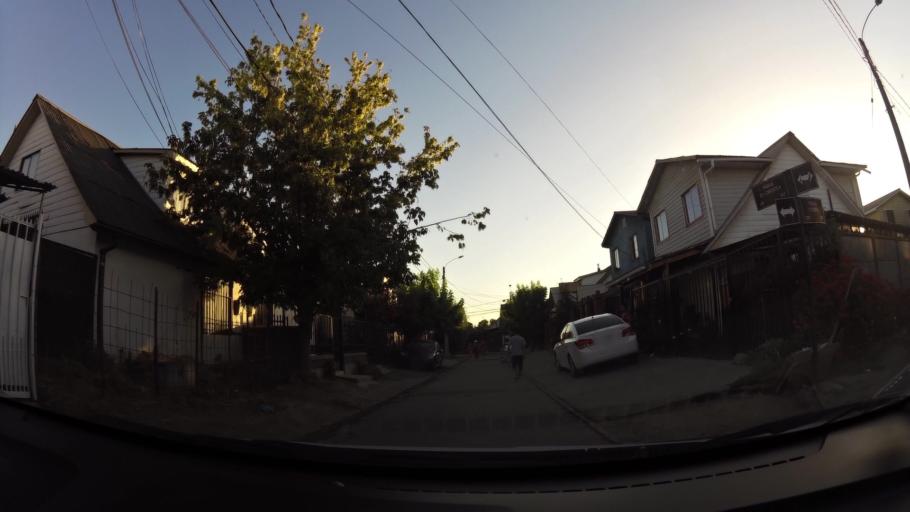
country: CL
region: Maule
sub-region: Provincia de Talca
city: Talca
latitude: -35.4406
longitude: -71.6371
